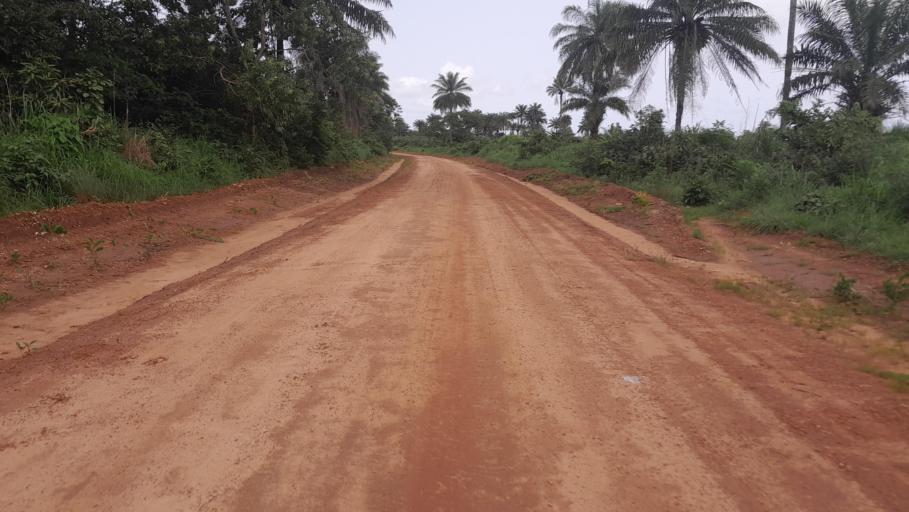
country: GN
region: Boke
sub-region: Boffa
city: Boffa
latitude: 10.0578
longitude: -13.8691
